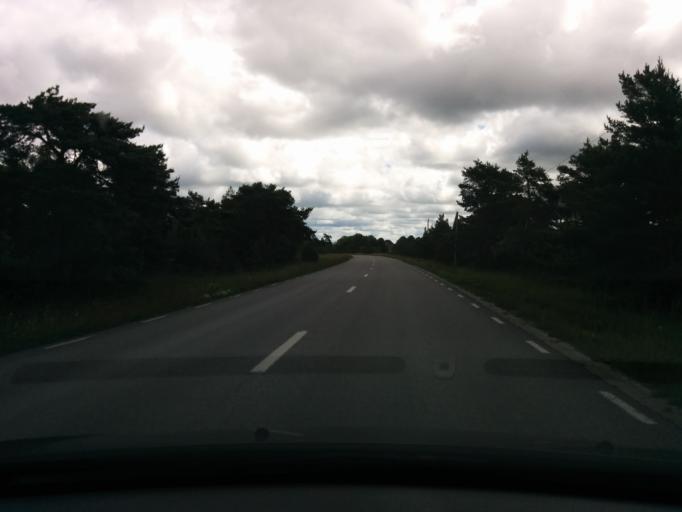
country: SE
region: Gotland
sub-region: Gotland
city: Visby
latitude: 57.6302
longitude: 18.4337
